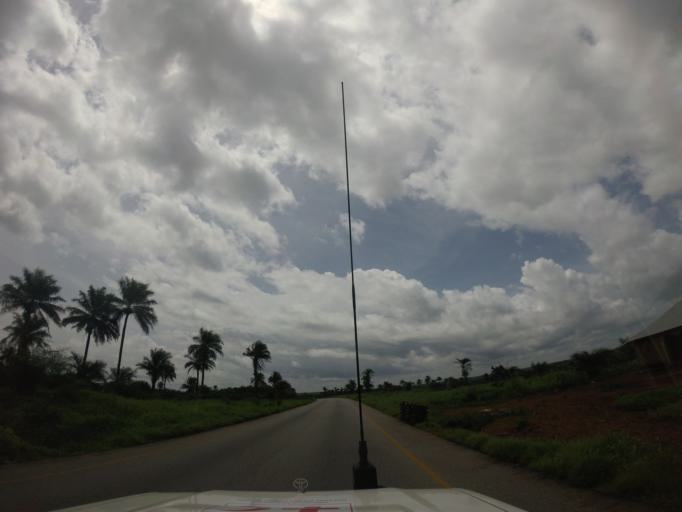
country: SL
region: Northern Province
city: Lunsar
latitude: 8.4776
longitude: -12.6470
